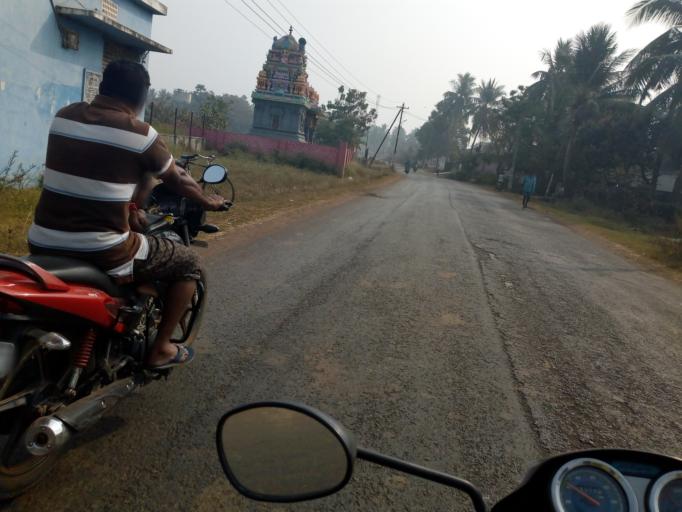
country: IN
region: Andhra Pradesh
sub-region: West Godavari
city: Tadepallegudem
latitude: 16.7762
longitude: 81.4229
